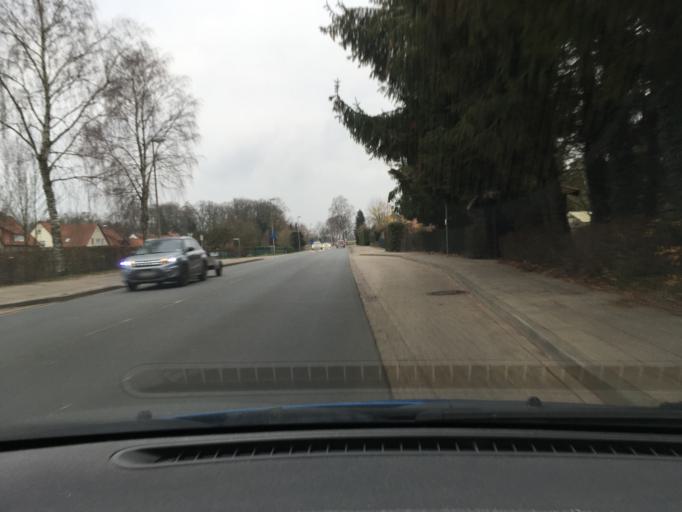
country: DE
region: Lower Saxony
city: Bad Fallingbostel
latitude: 52.8969
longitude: 9.7559
